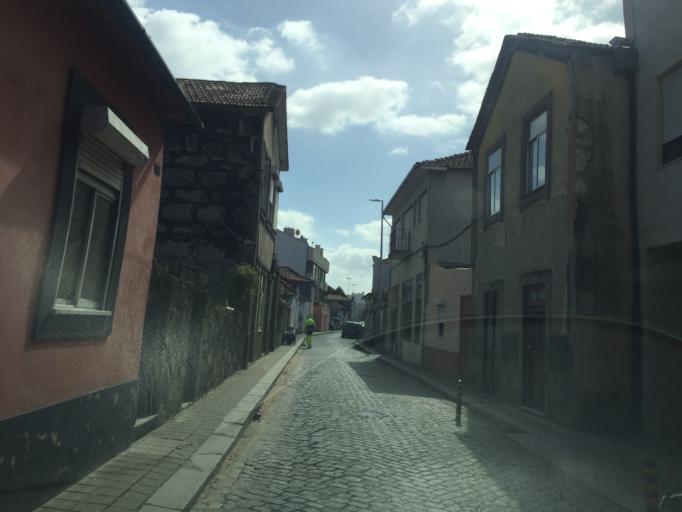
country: PT
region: Porto
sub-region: Matosinhos
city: Senhora da Hora
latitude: 41.1745
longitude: -8.6558
